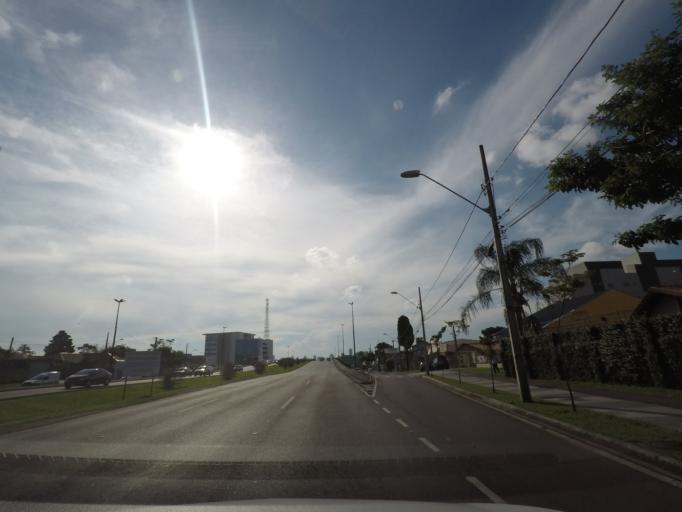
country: BR
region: Parana
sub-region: Curitiba
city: Curitiba
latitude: -25.4549
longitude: -49.2417
